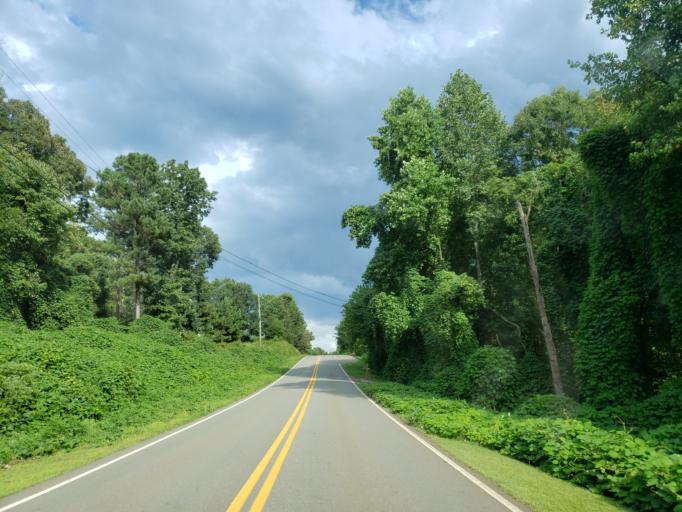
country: US
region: Georgia
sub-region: Pickens County
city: Jasper
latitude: 34.4099
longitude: -84.4869
